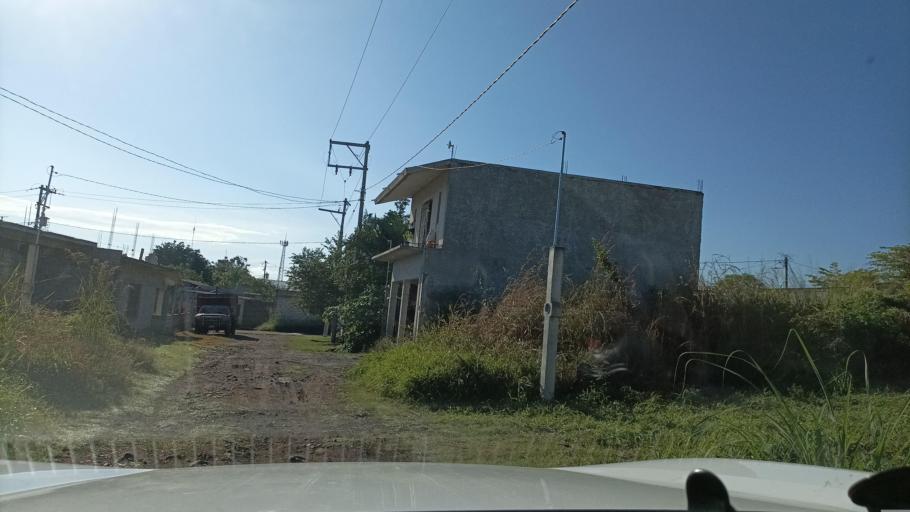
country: MX
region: Veracruz
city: Paso del Macho
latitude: 18.9798
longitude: -96.7296
